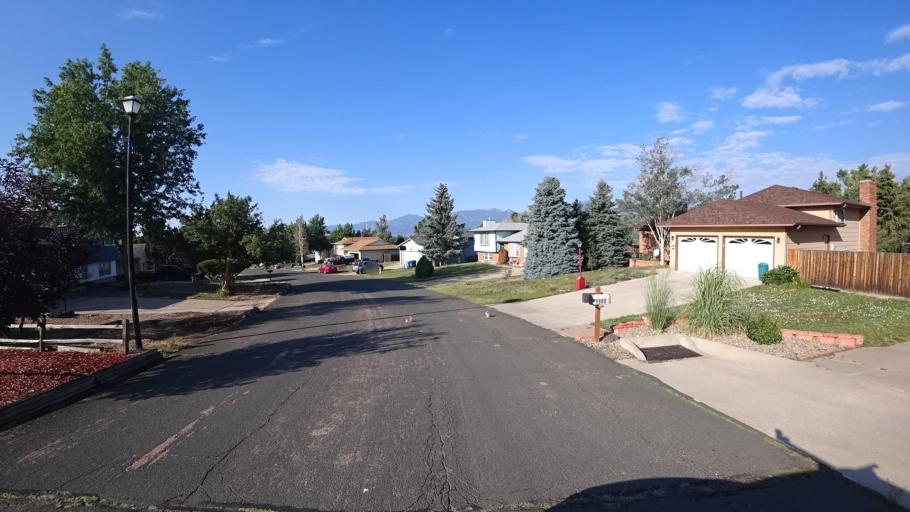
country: US
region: Colorado
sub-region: El Paso County
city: Air Force Academy
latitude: 38.9463
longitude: -104.7892
